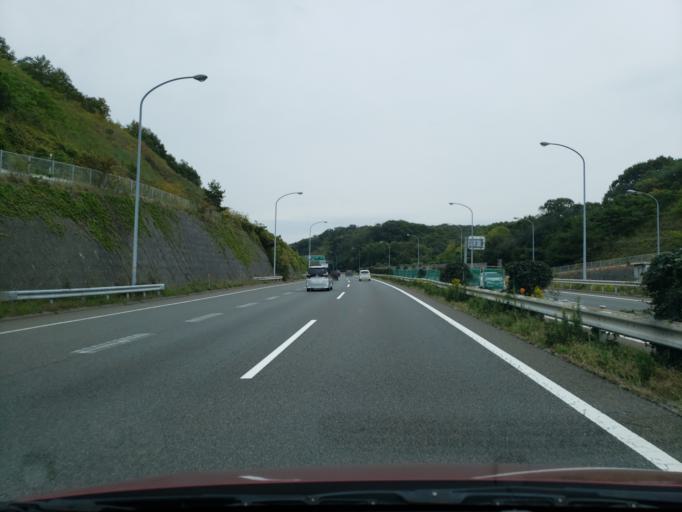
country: JP
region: Hyogo
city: Miki
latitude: 34.7982
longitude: 135.0555
